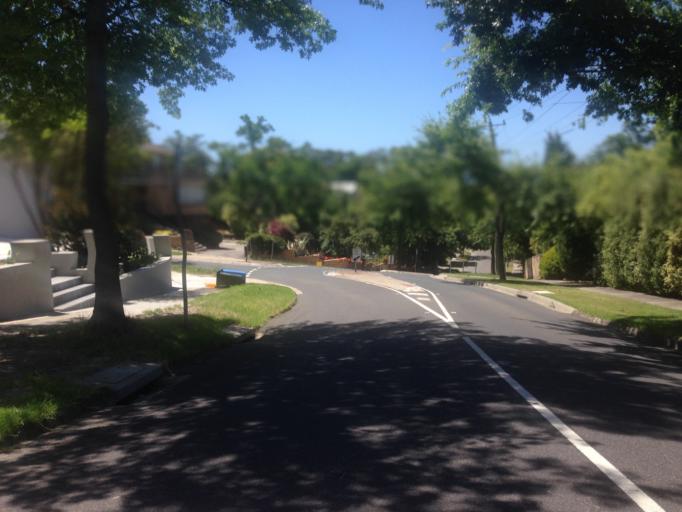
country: AU
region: Victoria
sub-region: Boroondara
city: Balwyn North
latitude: -37.7916
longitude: 145.0818
